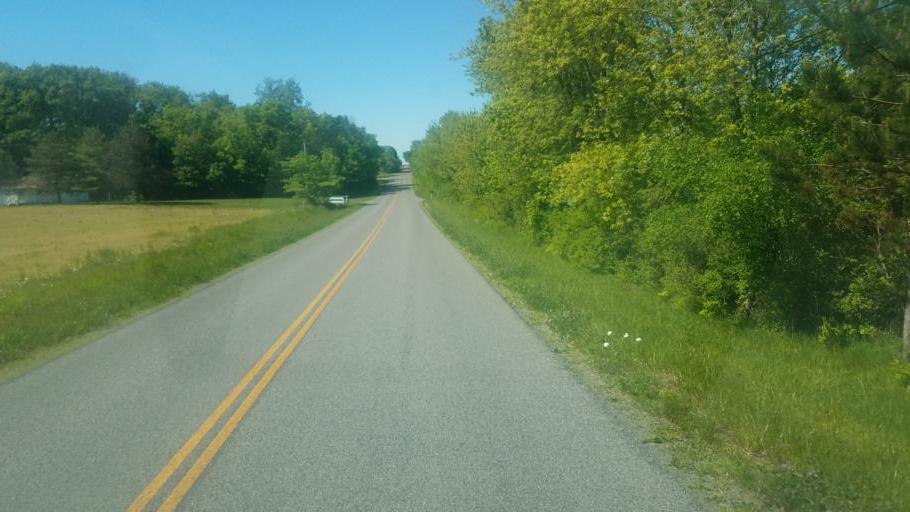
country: US
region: Ohio
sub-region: Logan County
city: Northwood
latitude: 40.4311
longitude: -83.7557
